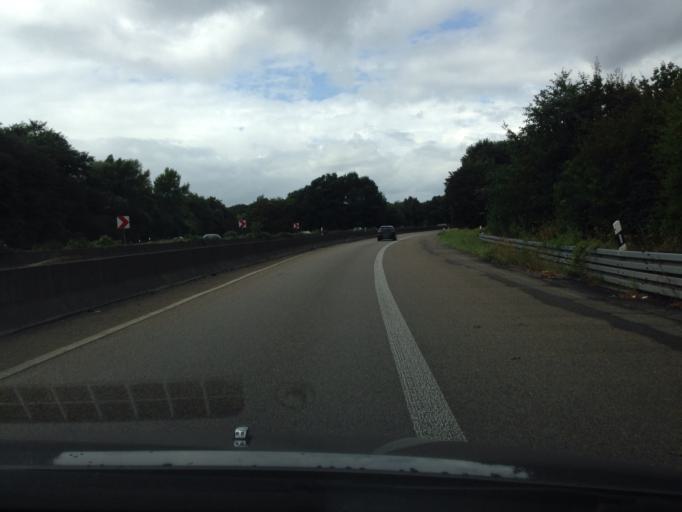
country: DE
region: North Rhine-Westphalia
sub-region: Regierungsbezirk Koln
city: Ostheim
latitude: 50.9140
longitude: 7.0302
